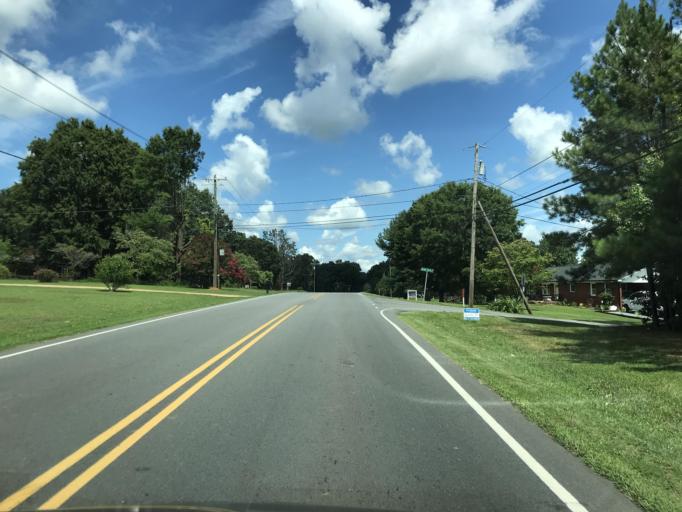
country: US
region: North Carolina
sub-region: Lincoln County
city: Pumpkin Center
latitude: 35.5024
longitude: -81.1830
